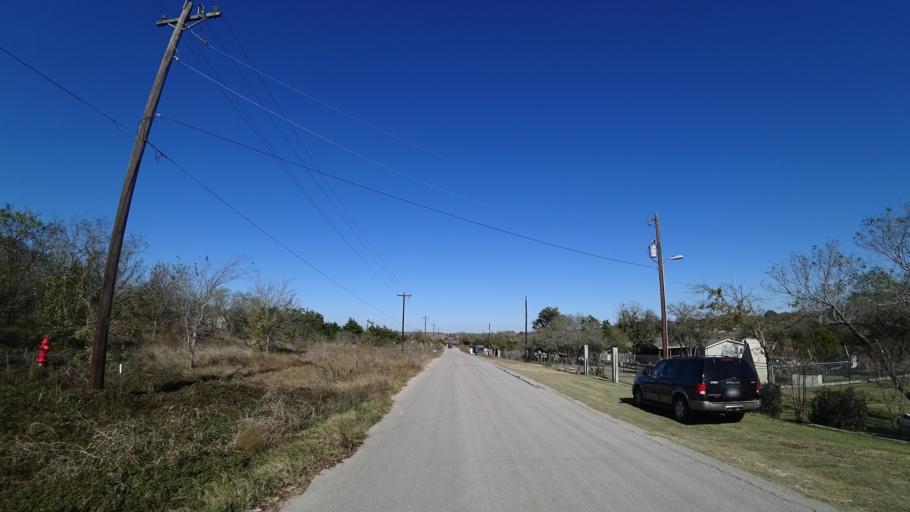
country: US
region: Texas
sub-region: Travis County
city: Garfield
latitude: 30.1003
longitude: -97.5986
